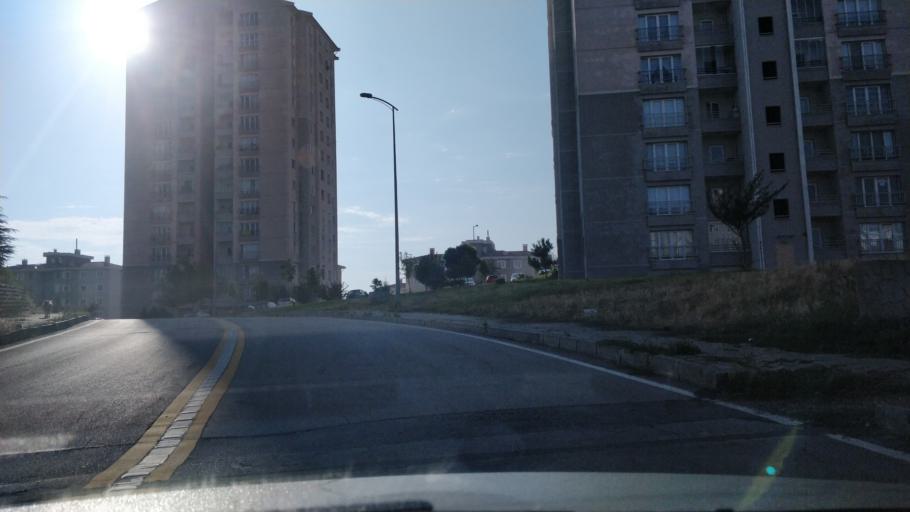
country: TR
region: Ankara
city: Etimesgut
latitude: 39.8427
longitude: 32.5417
